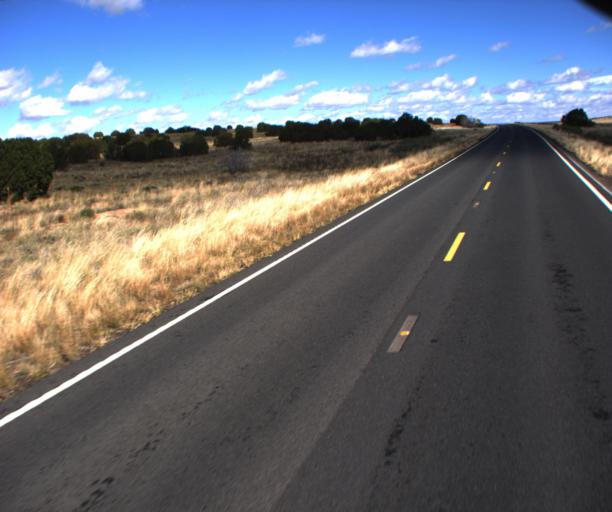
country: US
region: Arizona
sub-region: Apache County
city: Houck
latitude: 34.9582
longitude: -109.2291
